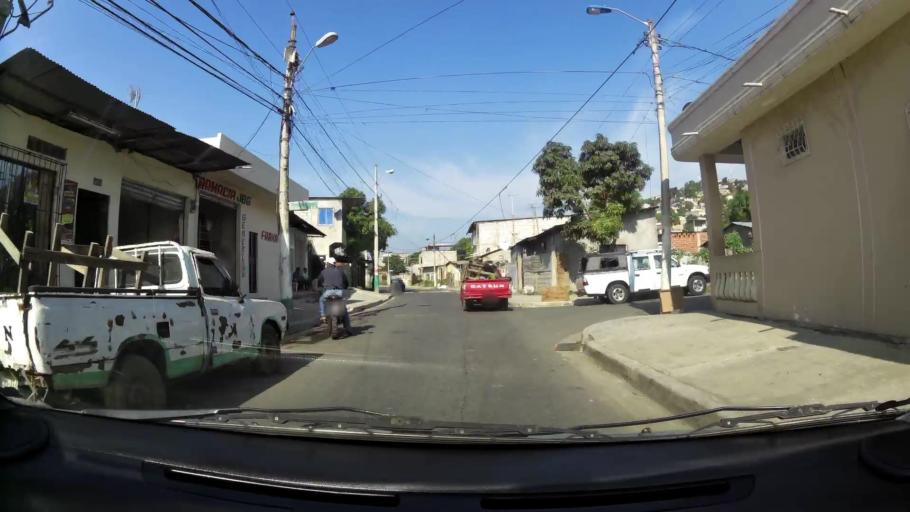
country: EC
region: Guayas
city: Eloy Alfaro
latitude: -2.0800
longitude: -79.9265
